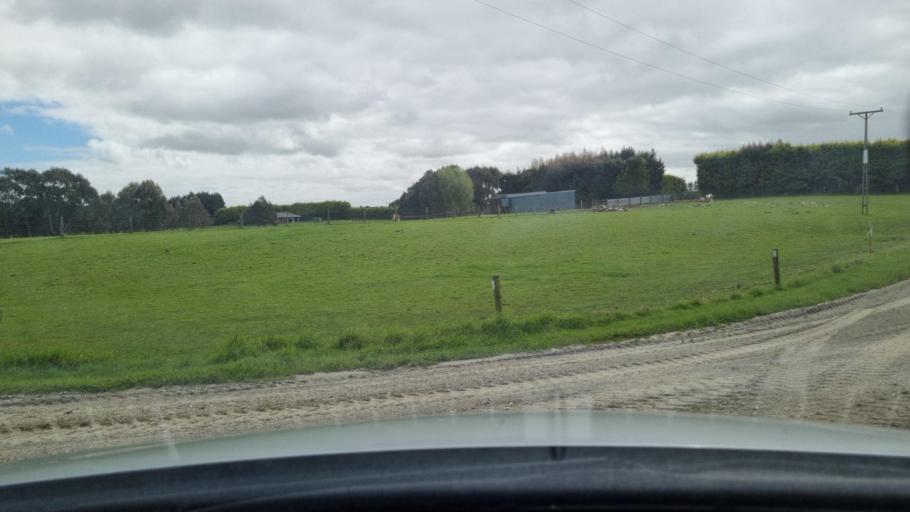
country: NZ
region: Southland
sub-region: Invercargill City
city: Invercargill
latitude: -46.4343
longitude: 168.4101
